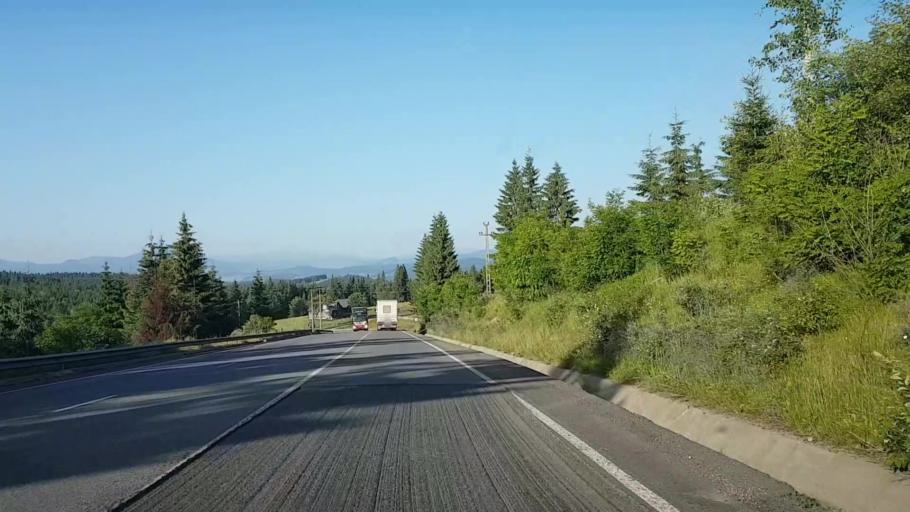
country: RO
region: Bistrita-Nasaud
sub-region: Comuna Lunca Ilvei
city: Lunca Ilvei
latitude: 47.2721
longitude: 25.0245
